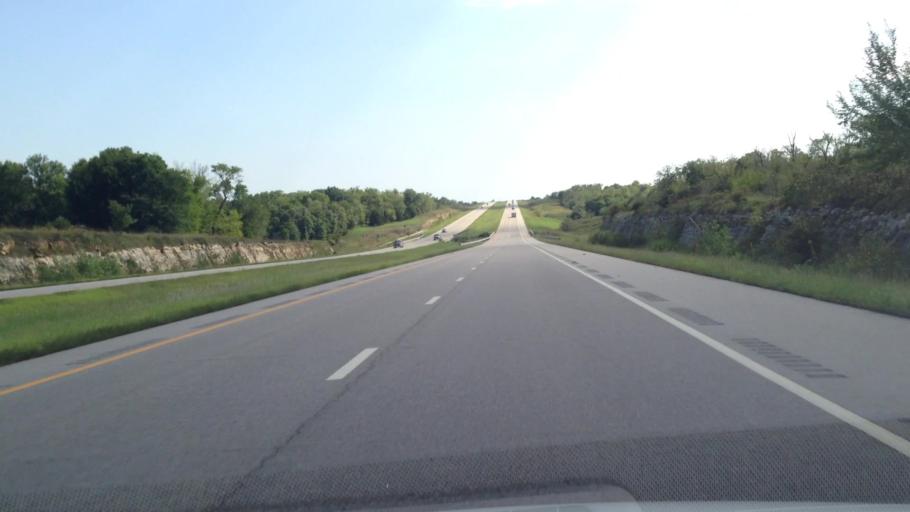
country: US
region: Kansas
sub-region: Linn County
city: La Cygne
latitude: 38.4355
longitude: -94.6870
